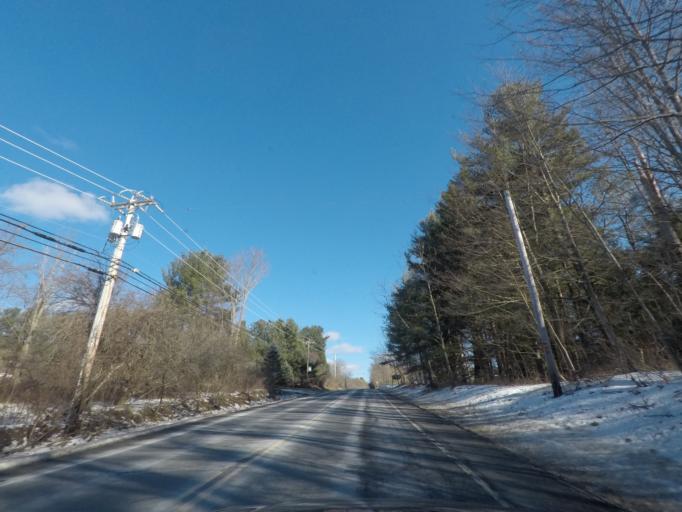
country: US
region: New York
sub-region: Columbia County
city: Chatham
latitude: 42.3204
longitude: -73.5350
